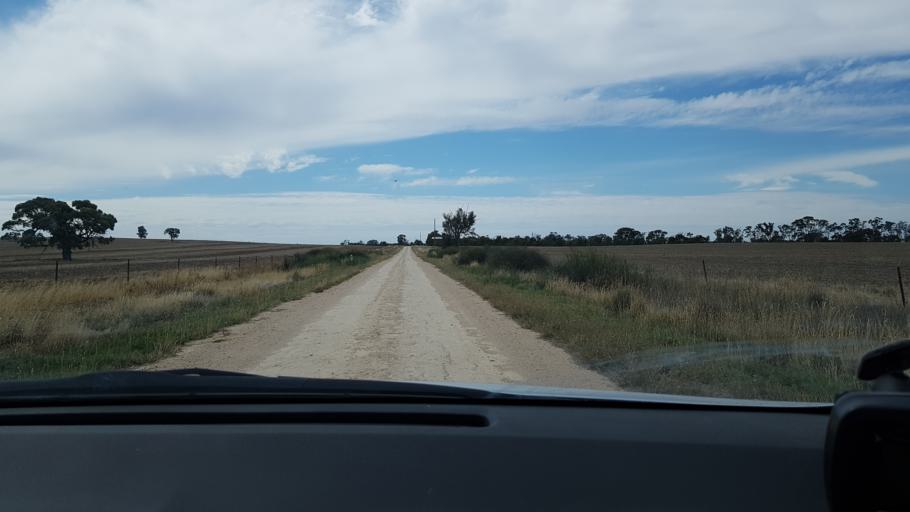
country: AU
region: Victoria
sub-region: Horsham
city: Horsham
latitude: -36.7044
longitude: 141.7808
